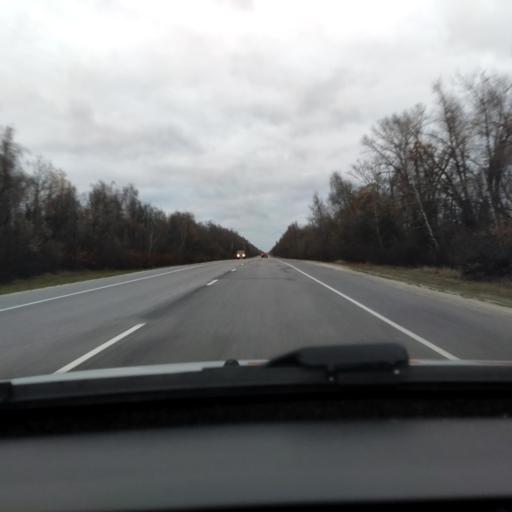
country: RU
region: Lipetsk
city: Khlevnoye
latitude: 52.2794
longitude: 39.1681
